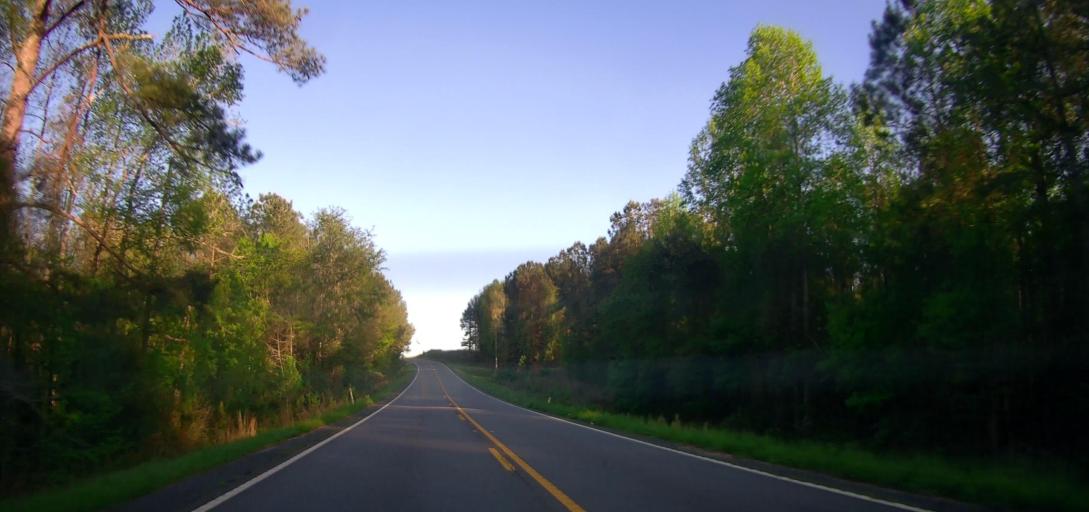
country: US
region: Georgia
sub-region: Schley County
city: Ellaville
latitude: 32.3475
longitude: -84.3741
